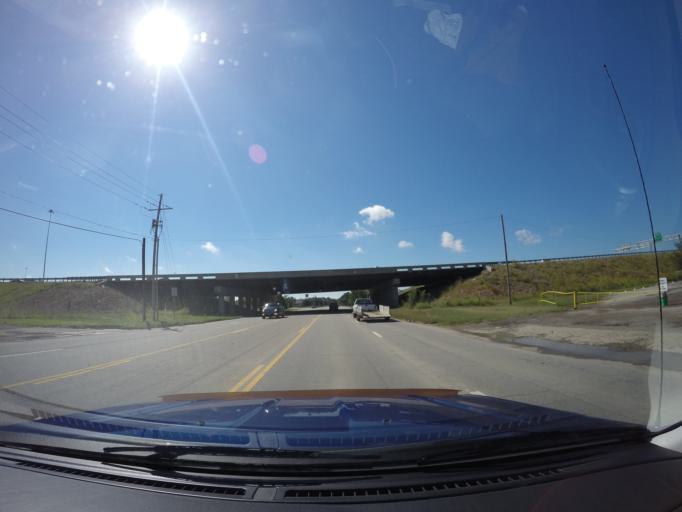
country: US
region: Kansas
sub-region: Douglas County
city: Lawrence
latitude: 38.9937
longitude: -95.2334
